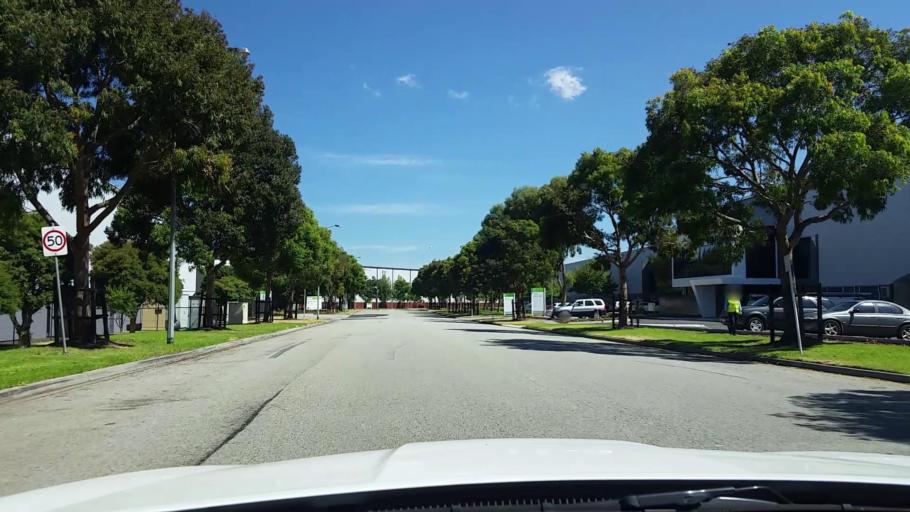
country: AU
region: Victoria
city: Heatherton
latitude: -37.9737
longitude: 145.1059
